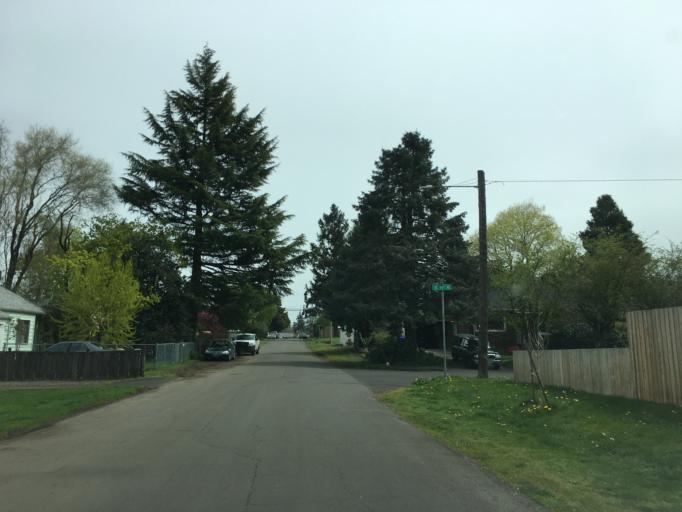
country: US
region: Oregon
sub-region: Multnomah County
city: Lents
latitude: 45.5573
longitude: -122.5771
